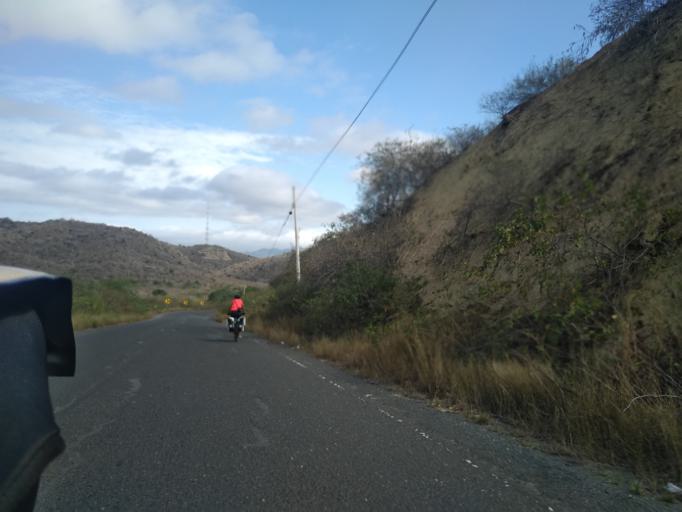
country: EC
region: Manabi
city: Jipijapa
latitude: -1.4514
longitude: -80.7597
